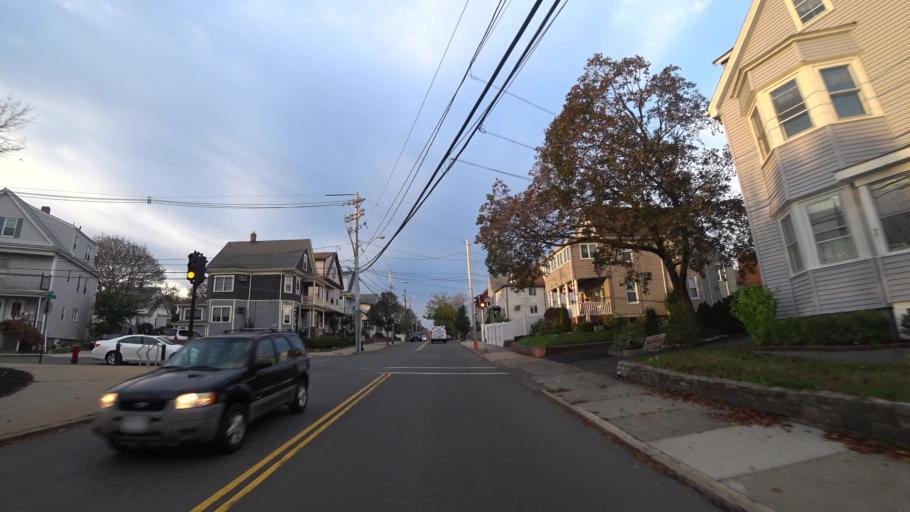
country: US
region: Massachusetts
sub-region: Middlesex County
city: Everett
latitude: 42.4224
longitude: -71.0419
